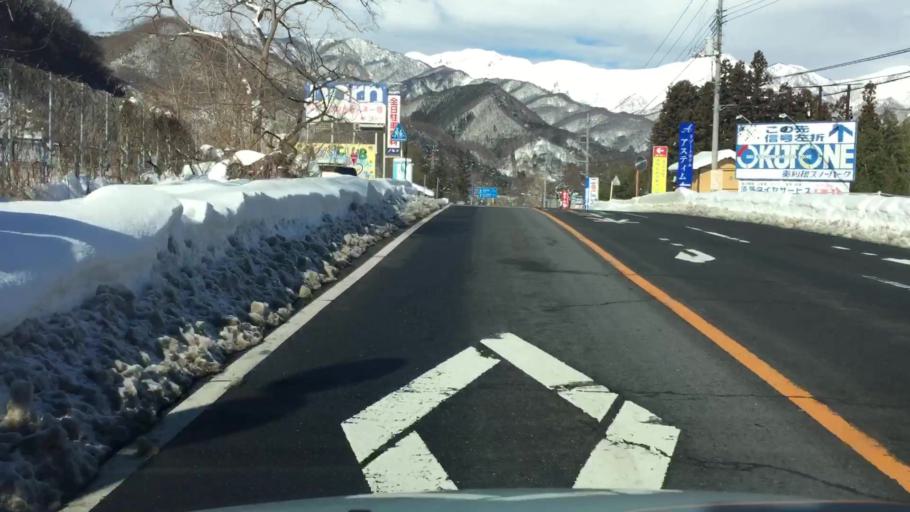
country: JP
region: Gunma
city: Numata
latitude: 36.7495
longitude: 138.9740
